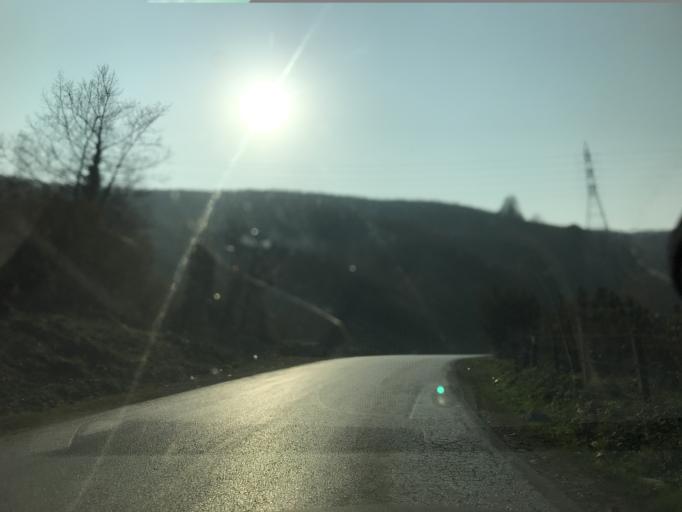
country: TR
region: Duzce
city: Cumayeri
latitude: 40.9023
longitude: 30.9547
